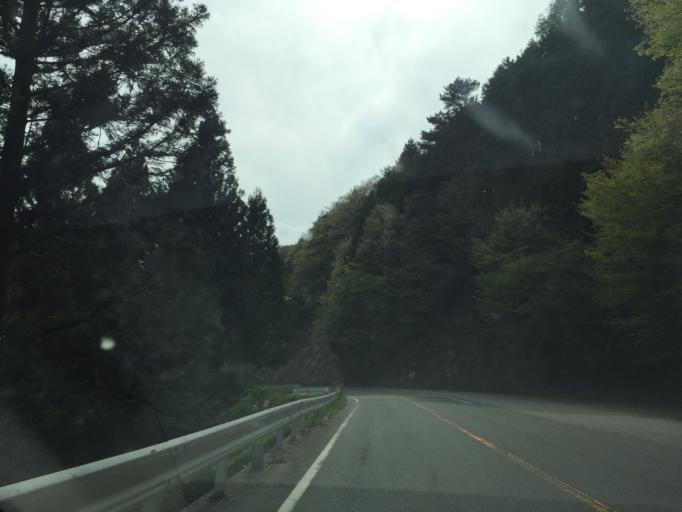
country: JP
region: Gifu
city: Nakatsugawa
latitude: 35.2191
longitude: 137.6891
